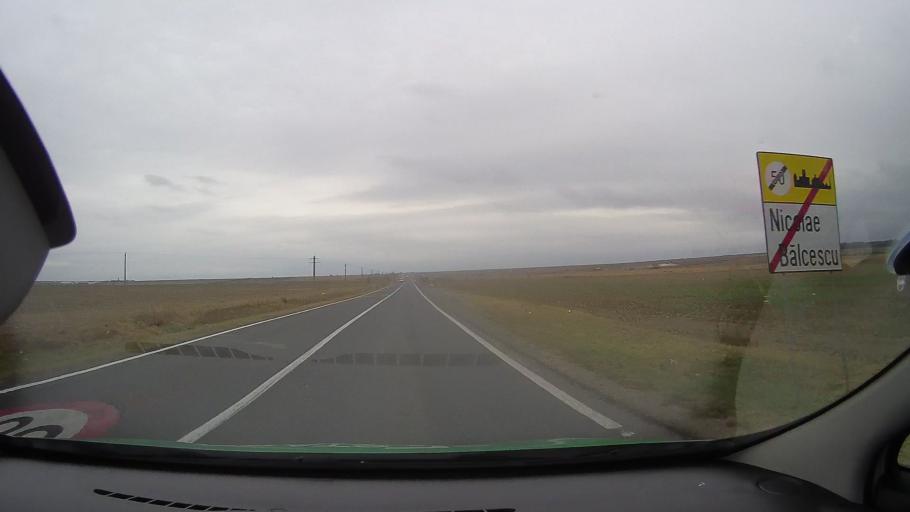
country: RO
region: Constanta
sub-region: Comuna Nicolae Balcescu
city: Nicolae Balcescu
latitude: 44.3871
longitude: 28.3869
